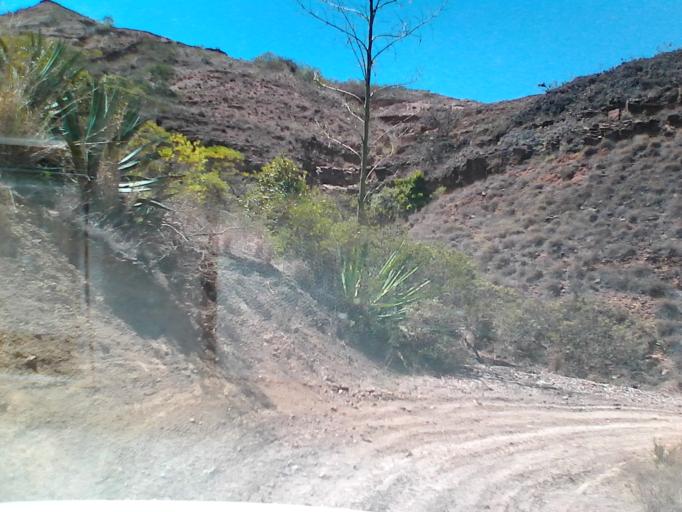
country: CO
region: Boyaca
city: Sachica
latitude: 5.6056
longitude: -73.5745
